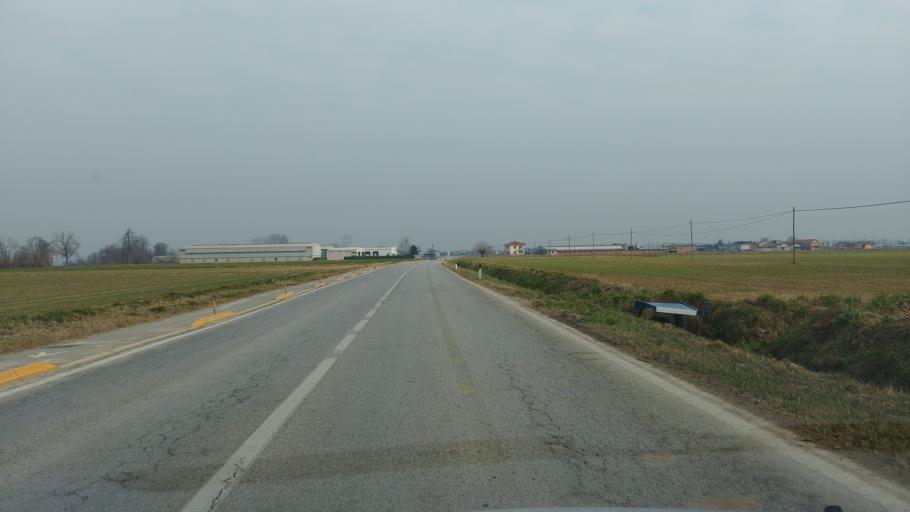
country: IT
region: Piedmont
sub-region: Provincia di Cuneo
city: Sant'Albano Stura
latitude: 44.4934
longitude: 7.7075
